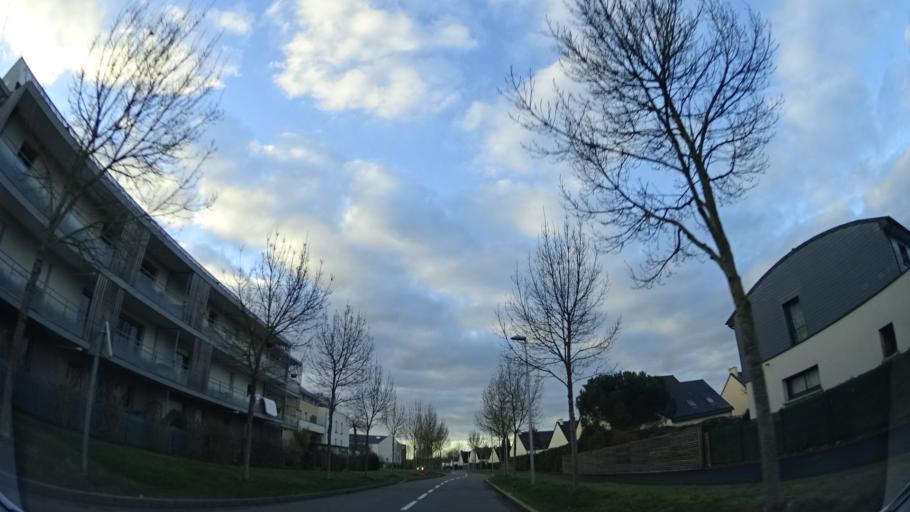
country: FR
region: Brittany
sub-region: Departement d'Ille-et-Vilaine
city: Betton
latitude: 48.1780
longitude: -1.6615
